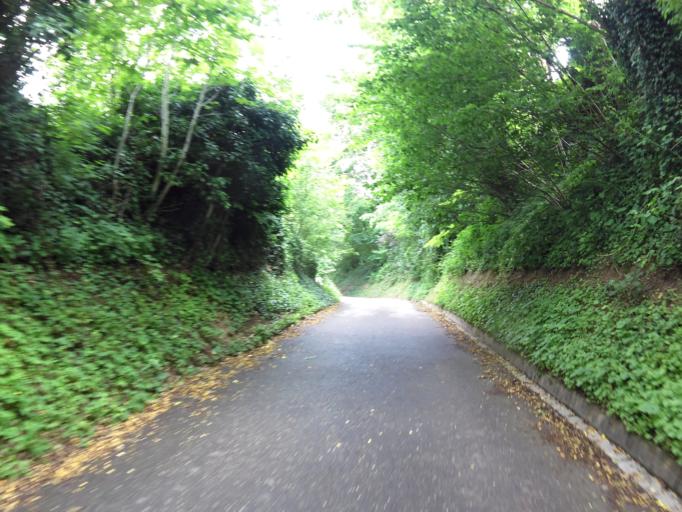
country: DE
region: Baden-Wuerttemberg
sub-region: Freiburg Region
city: Lahr
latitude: 48.3466
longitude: 7.8650
